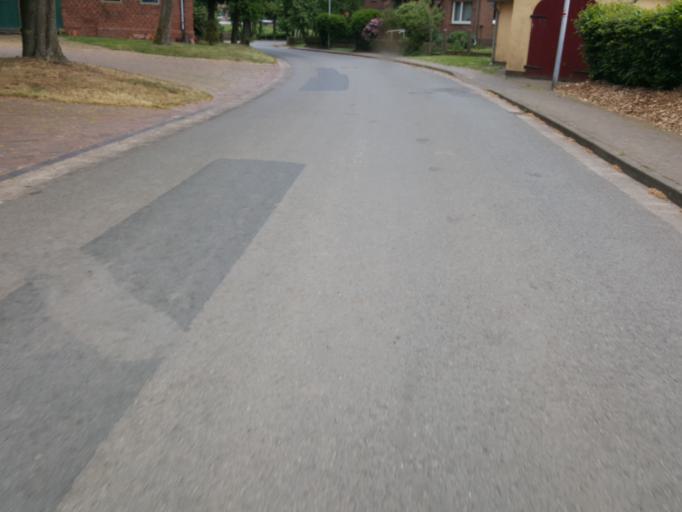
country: DE
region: Lower Saxony
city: Stolzenau
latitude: 52.5169
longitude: 9.0591
